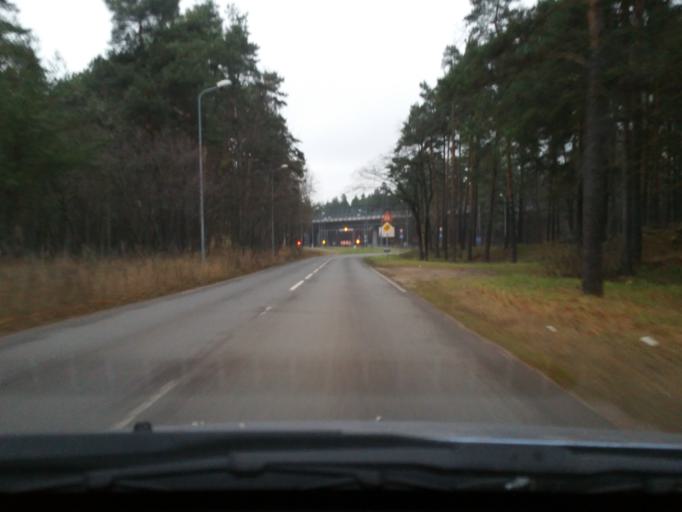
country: LV
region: Riga
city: Jaunciems
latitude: 56.9942
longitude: 24.1406
